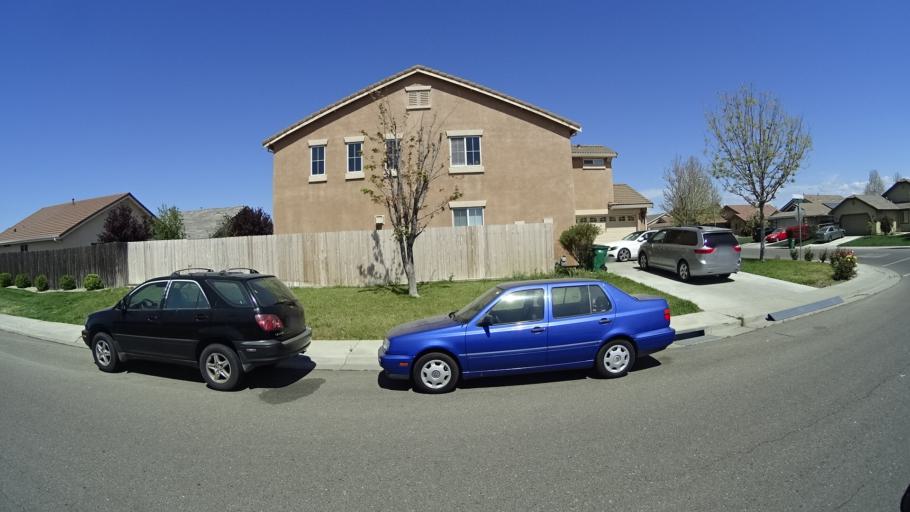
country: US
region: California
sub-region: Glenn County
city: Orland
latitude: 39.7449
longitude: -122.1714
